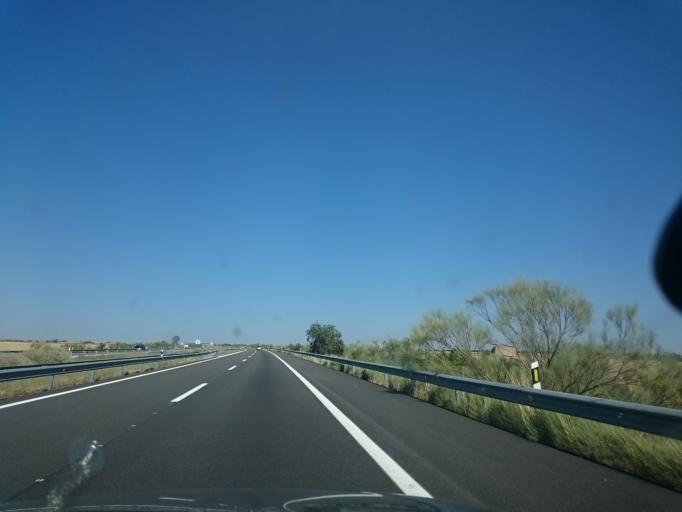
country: ES
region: Aragon
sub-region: Provincia de Zaragoza
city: Mequinensa / Mequinenza
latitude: 41.4674
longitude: 0.2399
